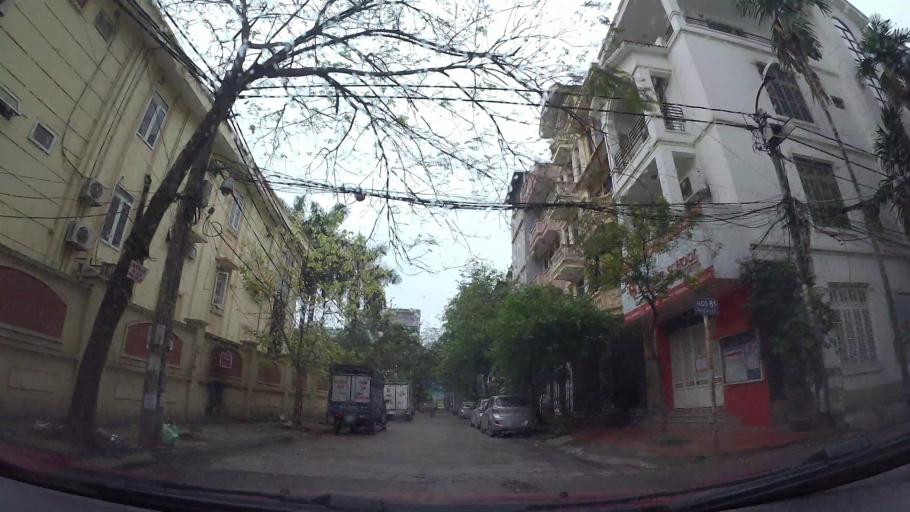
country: VN
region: Ha Noi
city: Dong Da
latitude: 21.0161
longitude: 105.8263
